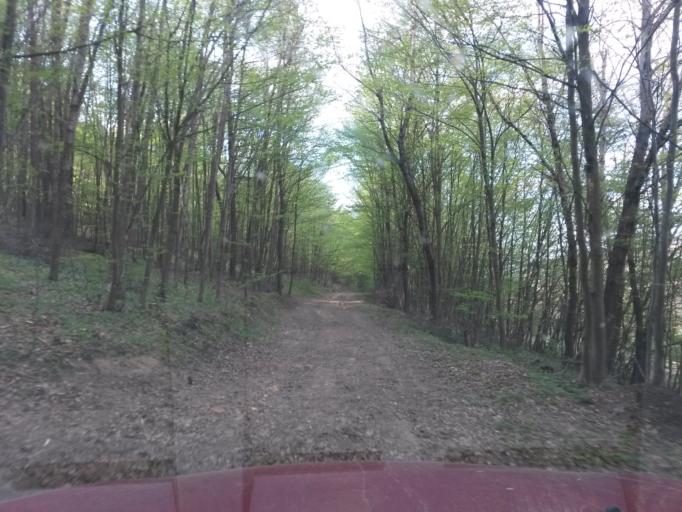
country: SK
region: Presovsky
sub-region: Okres Presov
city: Presov
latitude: 48.9501
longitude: 21.1575
